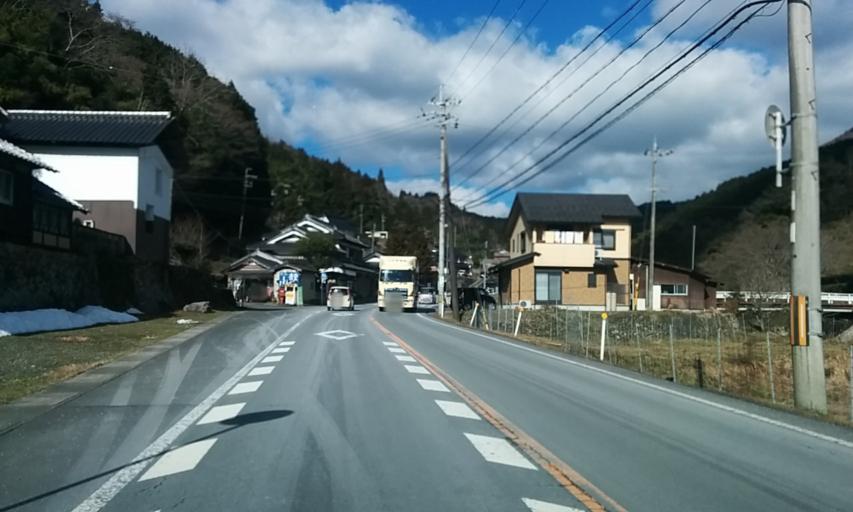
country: JP
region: Kyoto
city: Fukuchiyama
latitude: 35.3744
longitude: 135.0454
